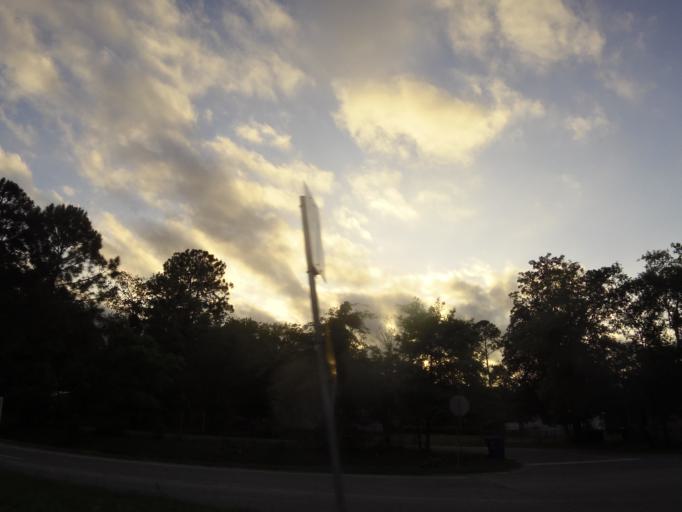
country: US
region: Florida
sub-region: Duval County
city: Jacksonville
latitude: 30.4506
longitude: -81.6131
